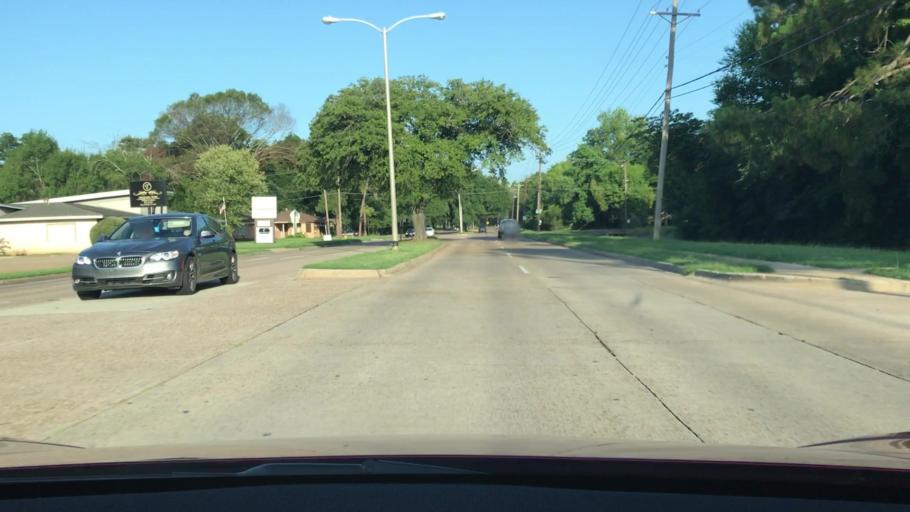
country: US
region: Louisiana
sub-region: Bossier Parish
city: Bossier City
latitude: 32.4567
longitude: -93.7234
